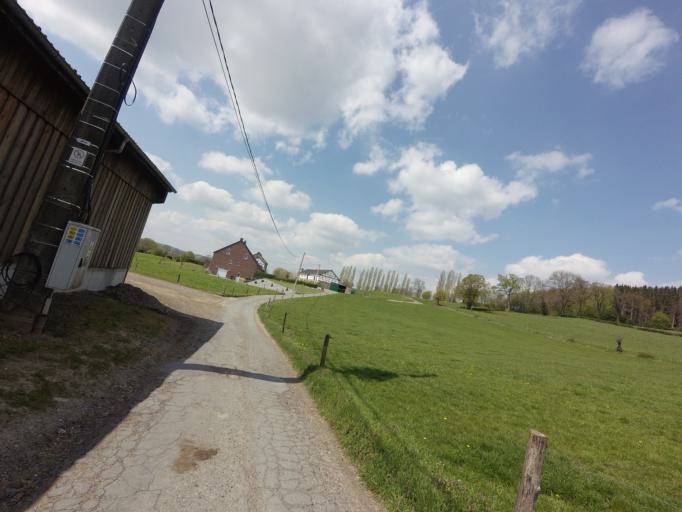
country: BE
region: Wallonia
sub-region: Province de Liege
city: Plombieres
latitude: 50.7565
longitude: 5.9566
